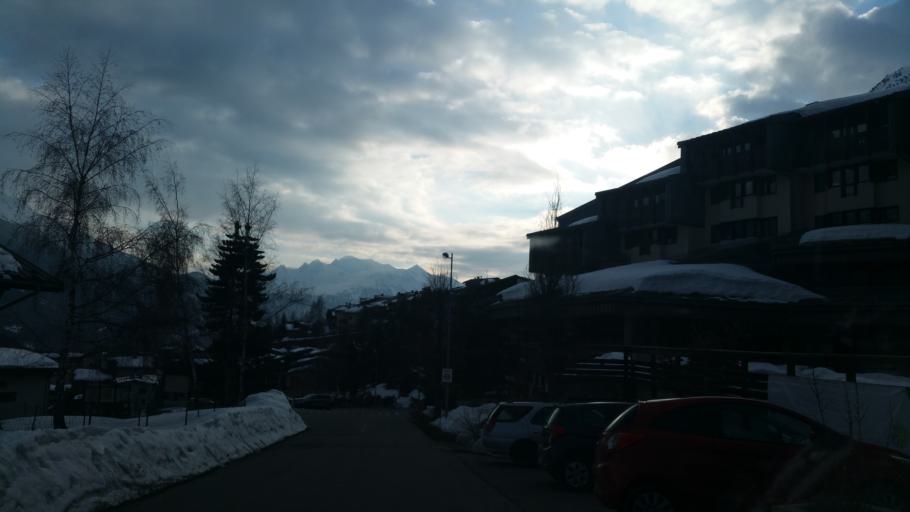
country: FR
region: Rhone-Alpes
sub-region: Departement de la Savoie
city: Modane
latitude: 45.2331
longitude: 6.7441
